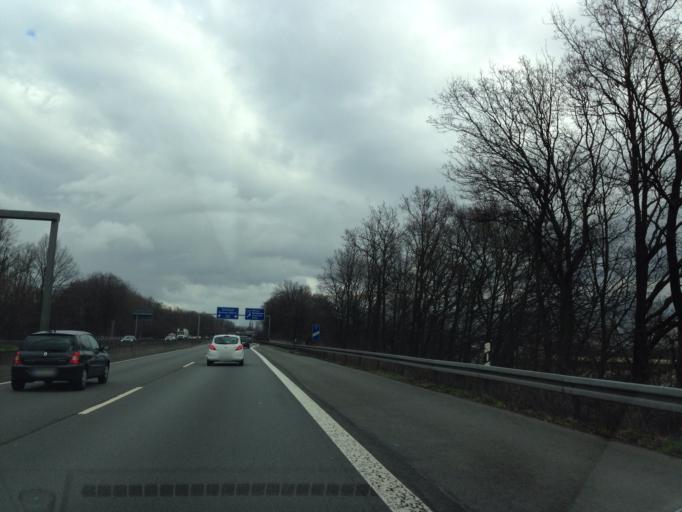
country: DE
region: North Rhine-Westphalia
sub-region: Regierungsbezirk Arnsberg
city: Bochum
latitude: 51.4950
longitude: 7.2607
